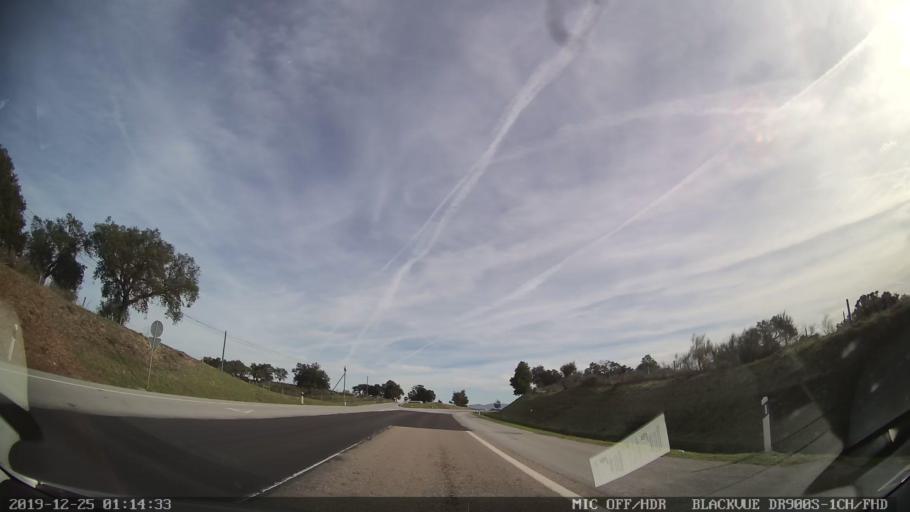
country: PT
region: Portalegre
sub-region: Nisa
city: Nisa
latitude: 39.4144
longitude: -7.6402
